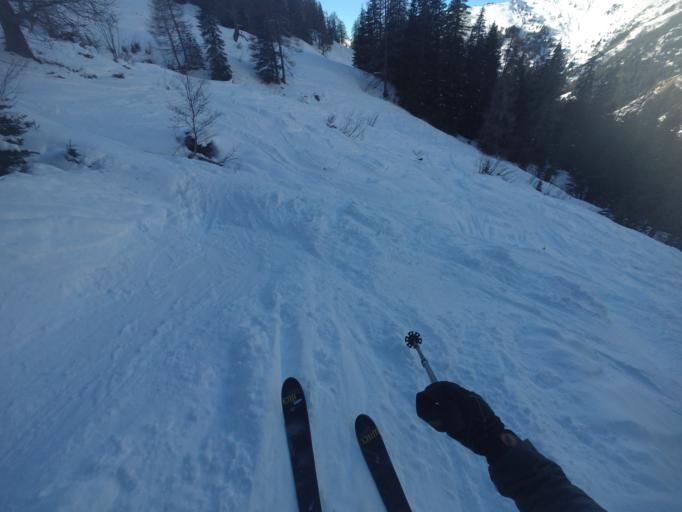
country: AT
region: Salzburg
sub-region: Politischer Bezirk Sankt Johann im Pongau
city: Huttschlag
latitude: 47.1826
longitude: 13.2850
